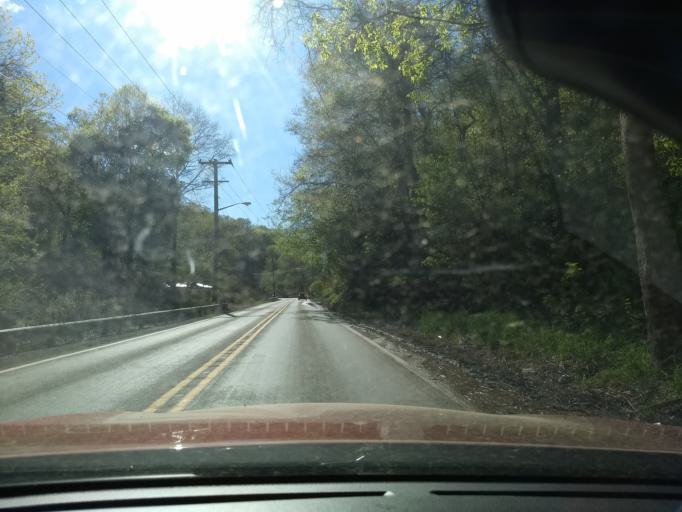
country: US
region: Pennsylvania
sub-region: Allegheny County
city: West Homestead
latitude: 40.3897
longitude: -79.9387
